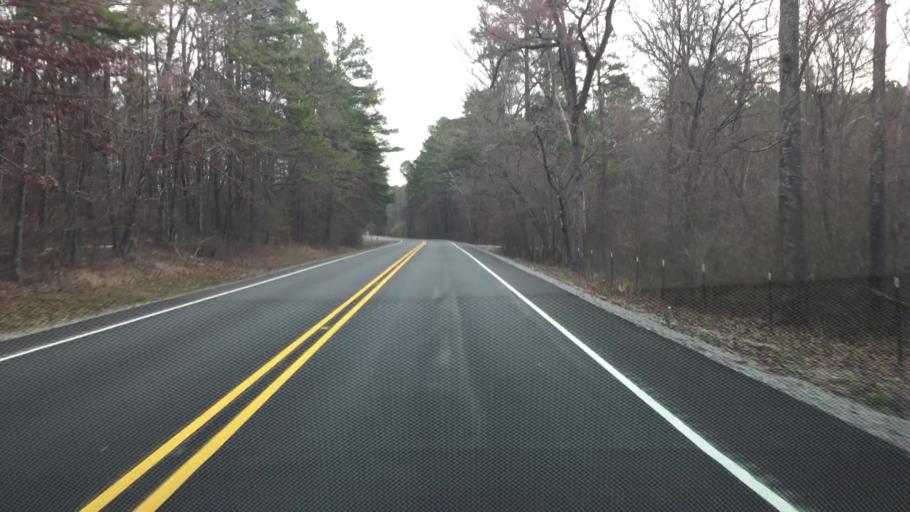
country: US
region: Arkansas
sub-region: Saline County
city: Haskell
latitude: 34.6128
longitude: -92.7943
